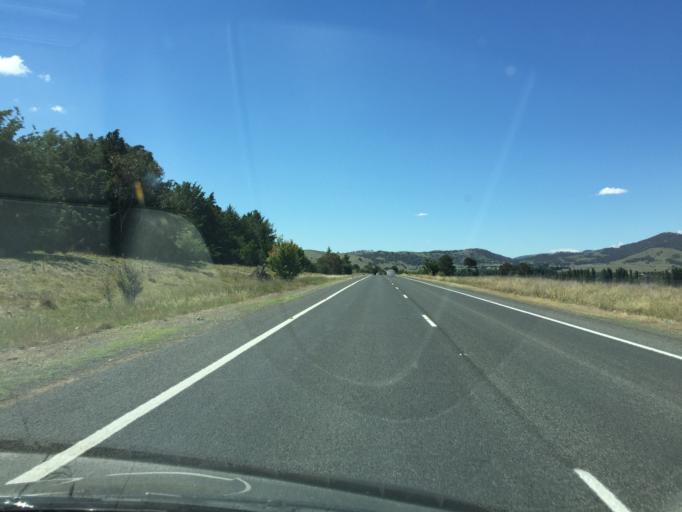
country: AU
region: Australian Capital Territory
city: Macarthur
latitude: -35.7263
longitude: 149.1597
